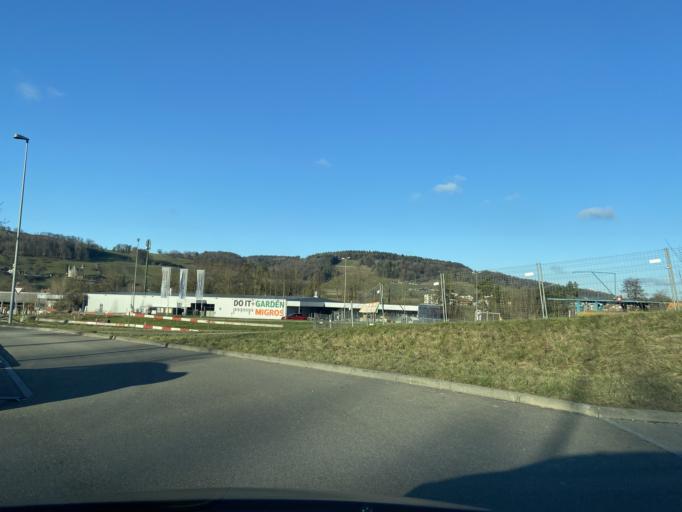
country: CH
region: Zurich
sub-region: Bezirk Winterthur
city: Pfungen
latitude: 47.5173
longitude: 8.6514
